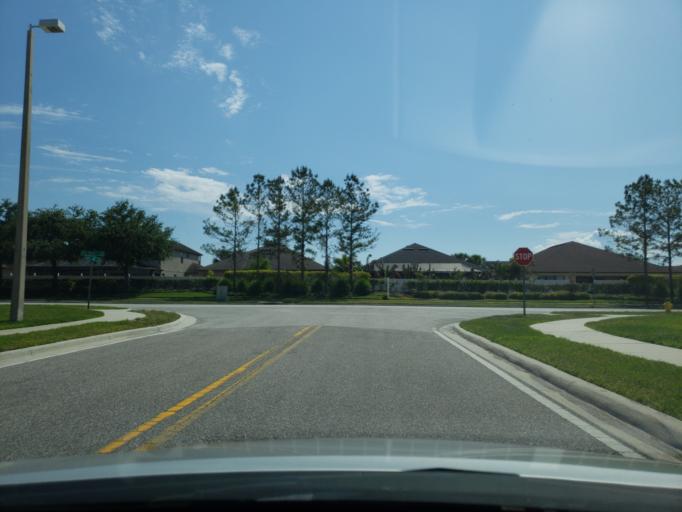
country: US
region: Florida
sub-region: Hillsborough County
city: Progress Village
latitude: 27.8732
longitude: -82.3606
